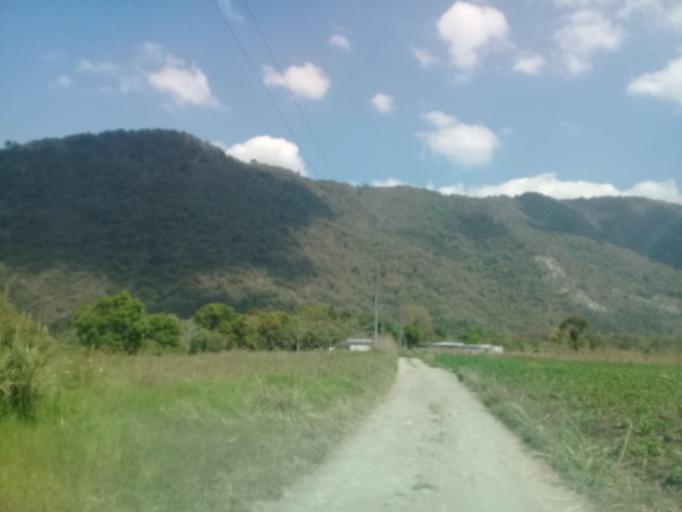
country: MX
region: Veracruz
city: Jalapilla
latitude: 18.8290
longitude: -97.0733
